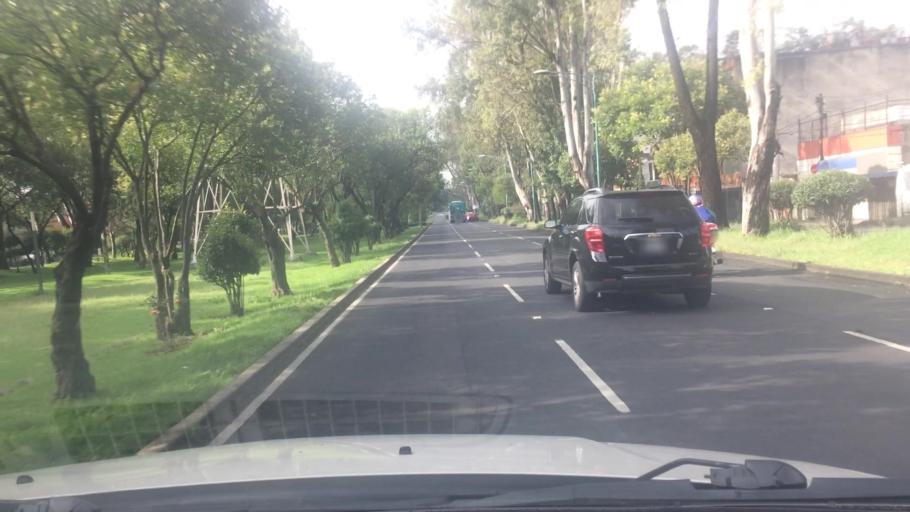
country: MX
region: Mexico City
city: Colonia Nativitas
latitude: 19.3554
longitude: -99.1303
